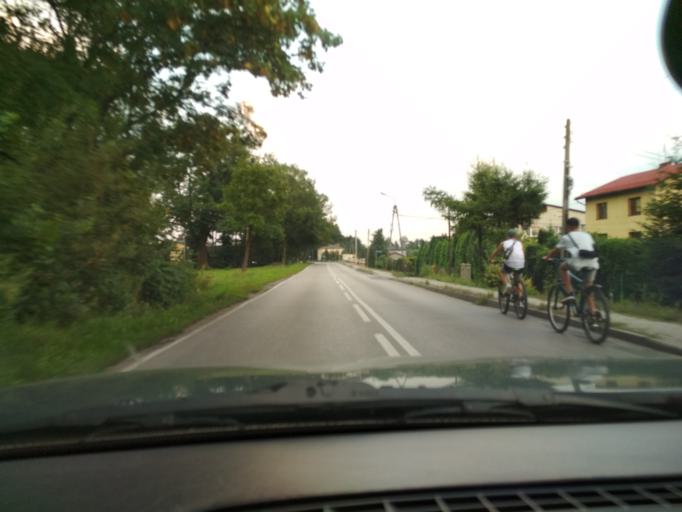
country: PL
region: Silesian Voivodeship
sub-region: Powiat cieszynski
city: Zablocie
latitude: 49.9003
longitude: 18.7882
